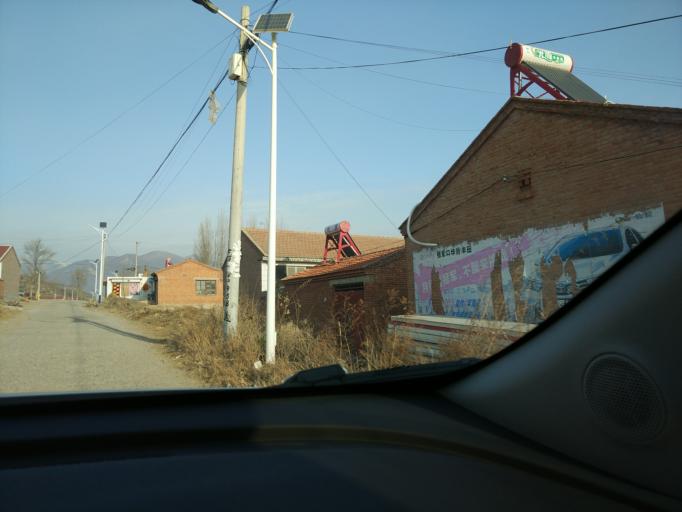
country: CN
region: Hebei
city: Xiwanzi
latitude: 40.8312
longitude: 115.5290
